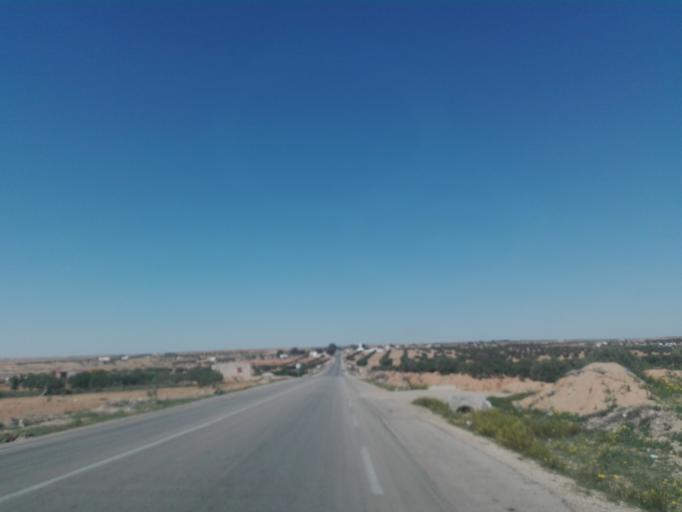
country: TN
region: Safaqis
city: Bi'r `Ali Bin Khalifah
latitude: 34.7411
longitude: 10.3820
